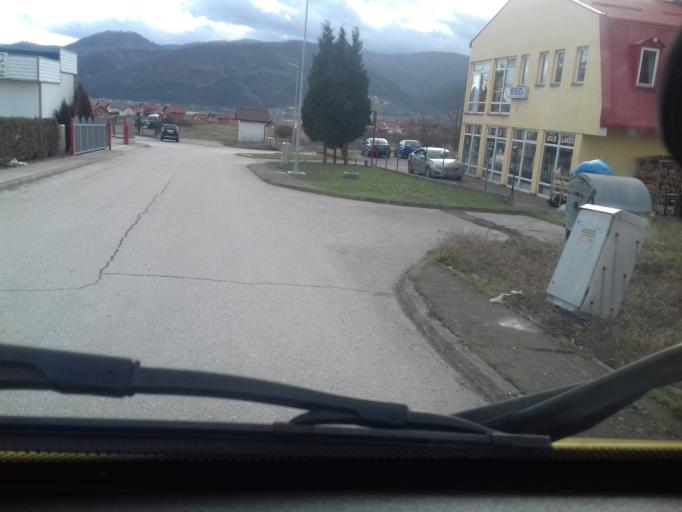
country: BA
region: Federation of Bosnia and Herzegovina
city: Zepce
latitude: 44.4378
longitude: 18.0430
